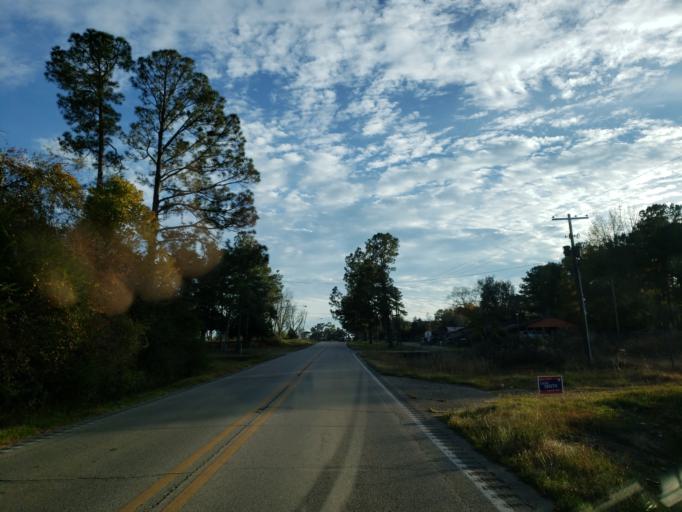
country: US
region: Mississippi
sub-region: Lamar County
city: Purvis
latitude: 31.1349
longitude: -89.4057
